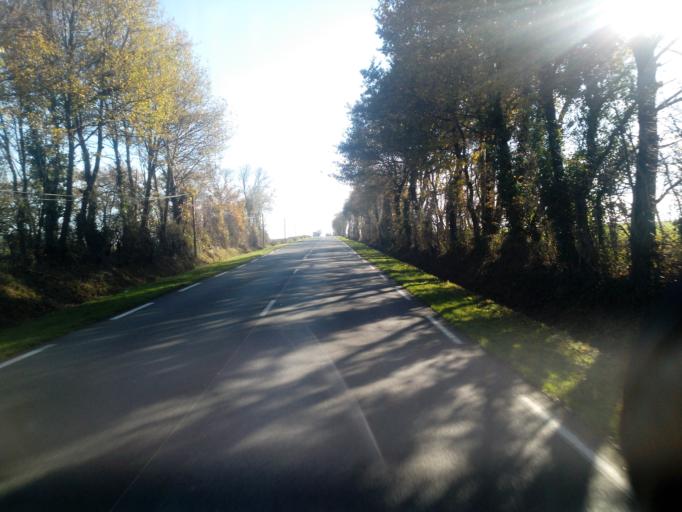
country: FR
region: Poitou-Charentes
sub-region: Departement de la Vienne
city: Saulge
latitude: 46.3229
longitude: 0.8193
